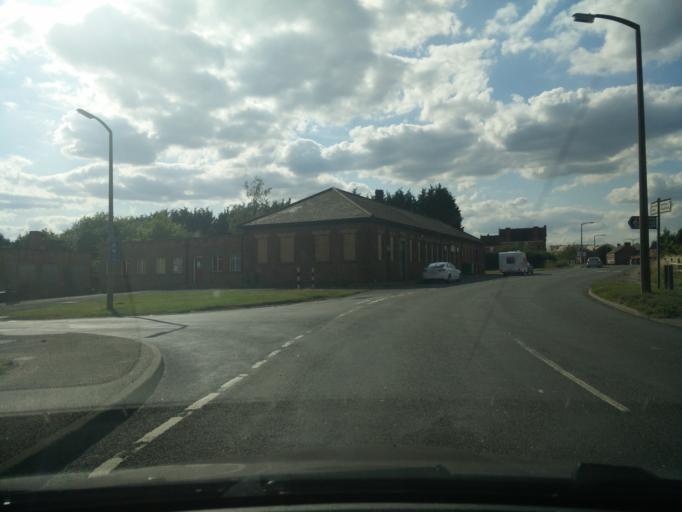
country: GB
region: England
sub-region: Derbyshire
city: Ilkeston
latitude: 52.9429
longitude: -1.2936
